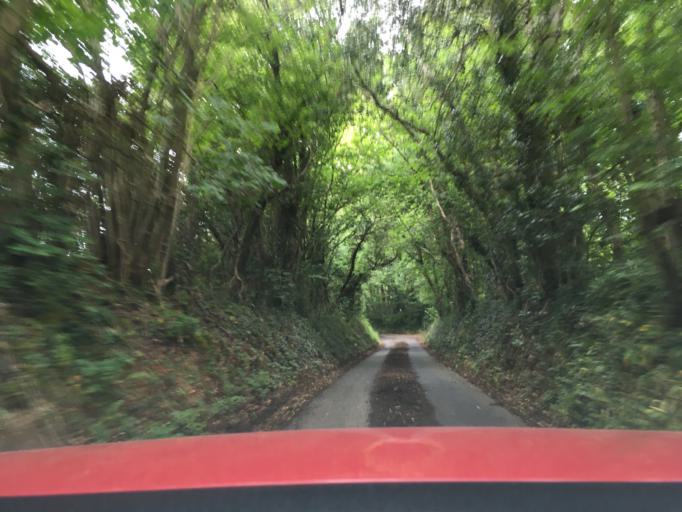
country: GB
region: England
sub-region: Gloucestershire
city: Shurdington
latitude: 51.7949
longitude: -2.0810
